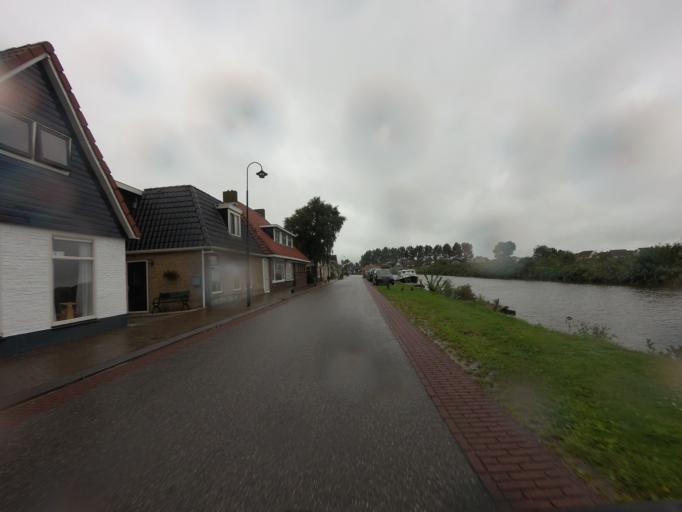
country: NL
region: Friesland
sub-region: Sudwest Fryslan
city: Workum
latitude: 53.0149
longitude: 5.4769
